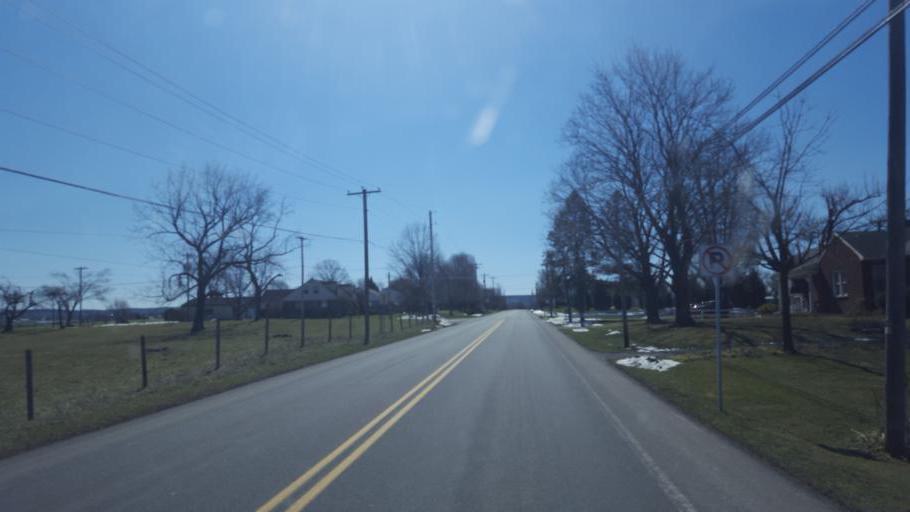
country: US
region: Pennsylvania
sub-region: Lancaster County
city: Blue Ball
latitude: 40.1380
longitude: -76.0288
